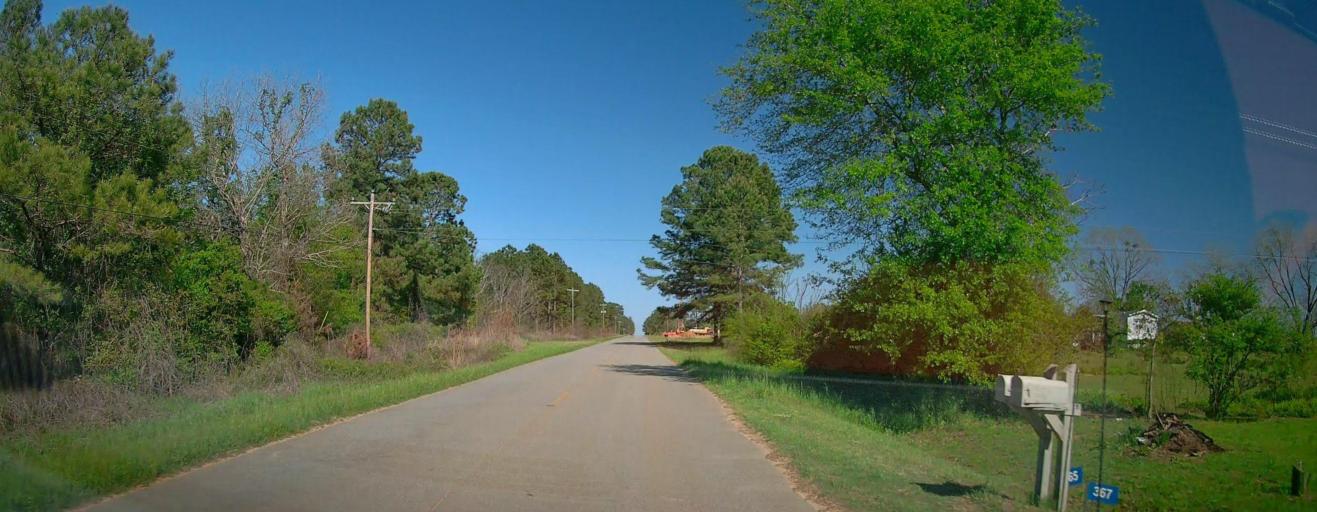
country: US
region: Georgia
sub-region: Pulaski County
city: Hawkinsville
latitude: 32.2405
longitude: -83.5349
